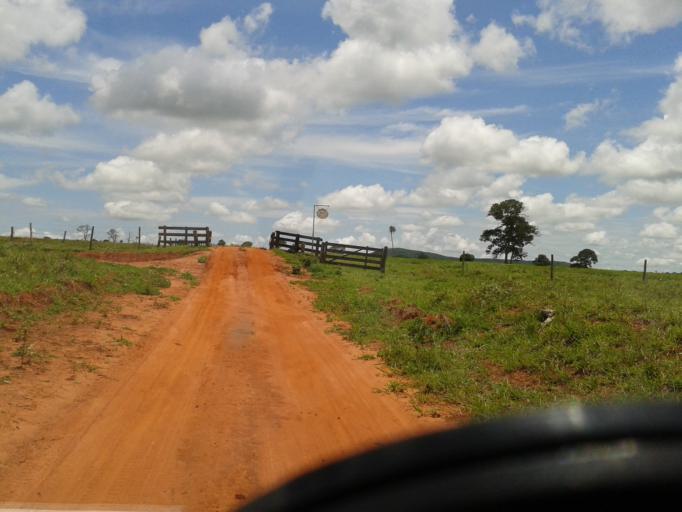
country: BR
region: Minas Gerais
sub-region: Santa Vitoria
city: Santa Vitoria
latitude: -19.0091
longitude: -49.9243
